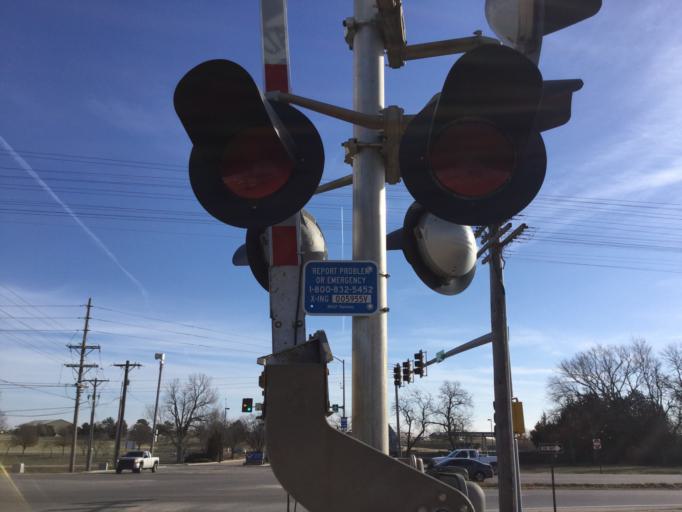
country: US
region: Kansas
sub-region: Shawnee County
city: Topeka
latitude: 38.9642
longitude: -95.6878
